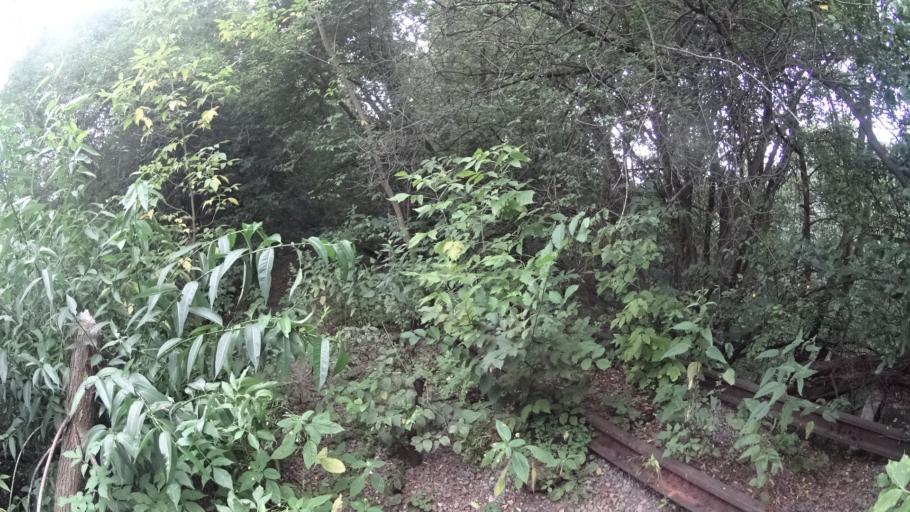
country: PL
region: Masovian Voivodeship
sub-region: Powiat grojecki
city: Mogielnica
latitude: 51.6677
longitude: 20.7445
